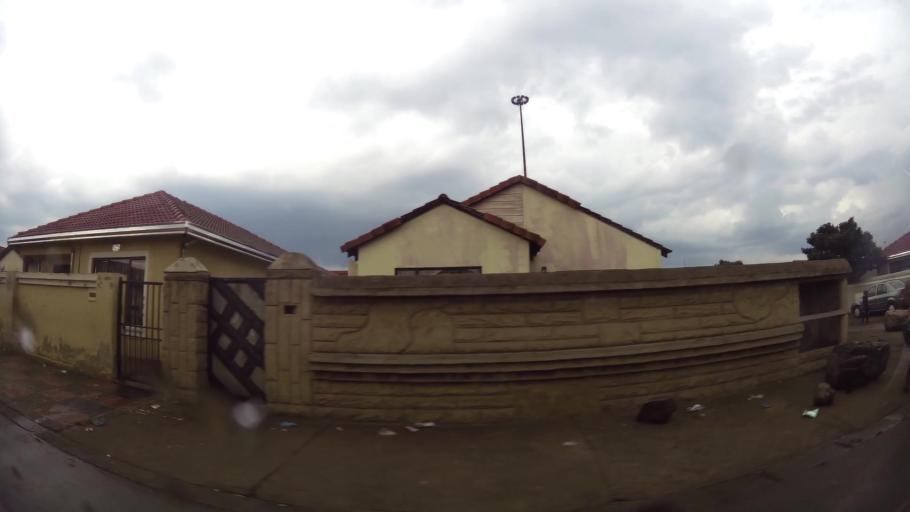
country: ZA
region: Gauteng
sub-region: Ekurhuleni Metropolitan Municipality
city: Germiston
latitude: -26.3684
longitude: 28.1351
